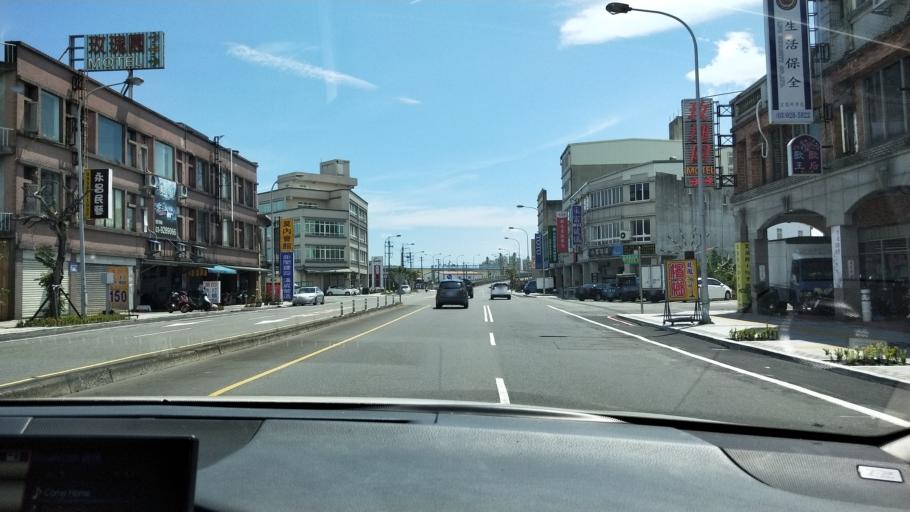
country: TW
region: Taiwan
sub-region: Yilan
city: Yilan
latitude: 24.7682
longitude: 121.7602
